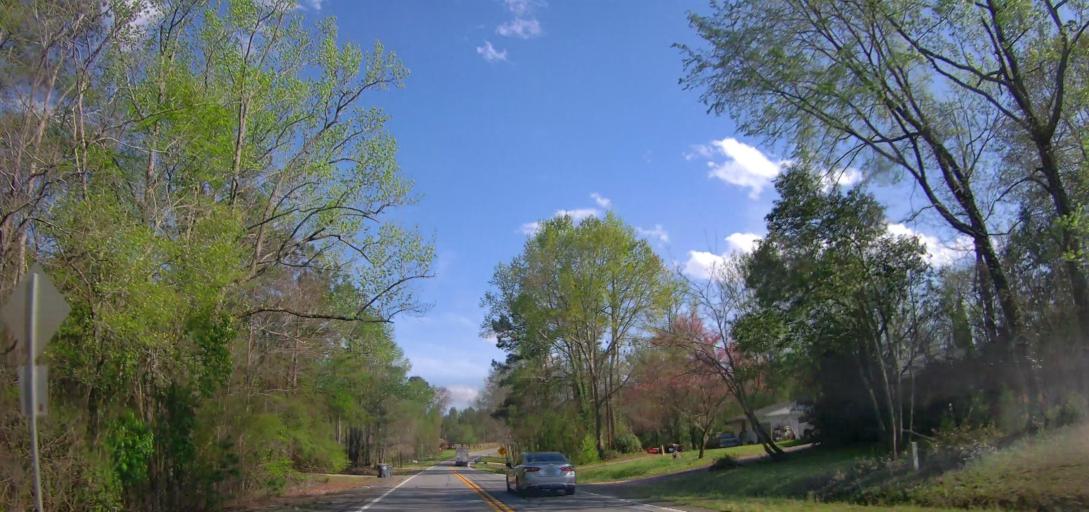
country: US
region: Georgia
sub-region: Baldwin County
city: Hardwick
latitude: 33.0883
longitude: -83.1735
